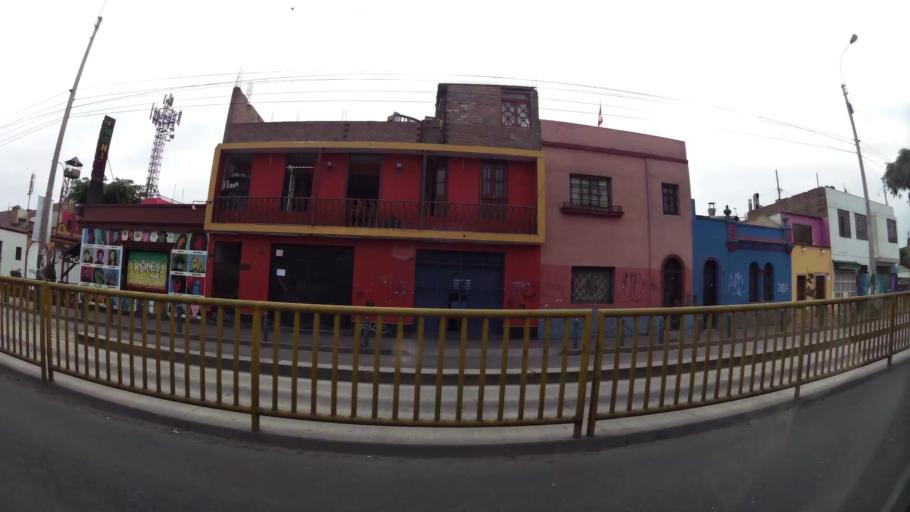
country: PE
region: Lima
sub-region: Lima
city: Surco
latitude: -12.1465
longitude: -77.0195
